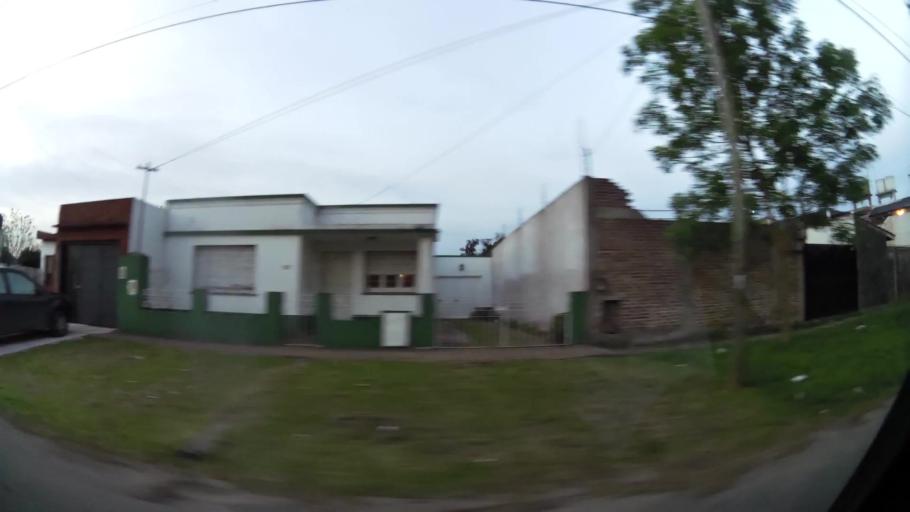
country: AR
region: Buenos Aires
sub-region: Partido de Quilmes
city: Quilmes
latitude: -34.8020
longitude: -58.2841
